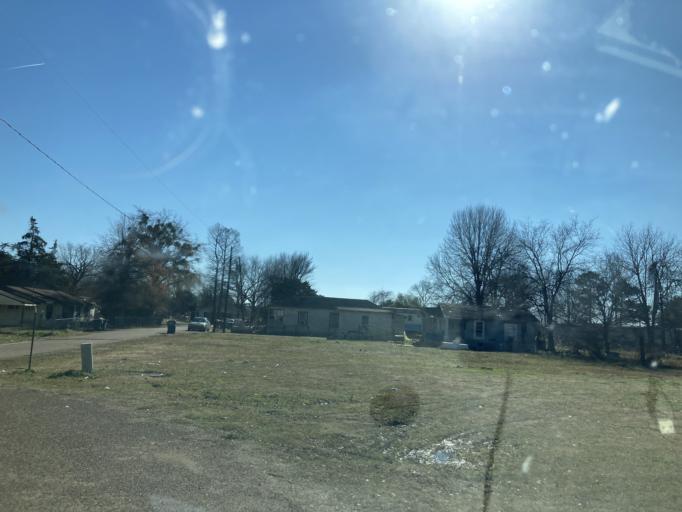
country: US
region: Mississippi
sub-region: Yazoo County
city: Yazoo City
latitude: 32.9768
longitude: -90.5928
